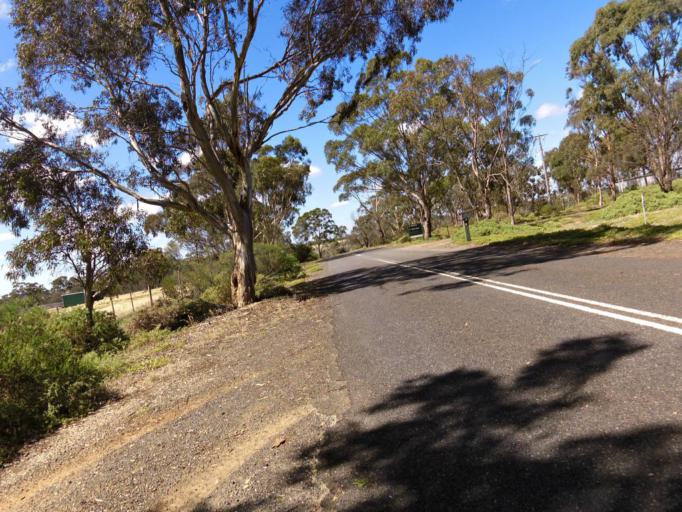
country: AU
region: Victoria
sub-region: Brimbank
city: Sydenham
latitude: -37.6701
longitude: 144.7649
